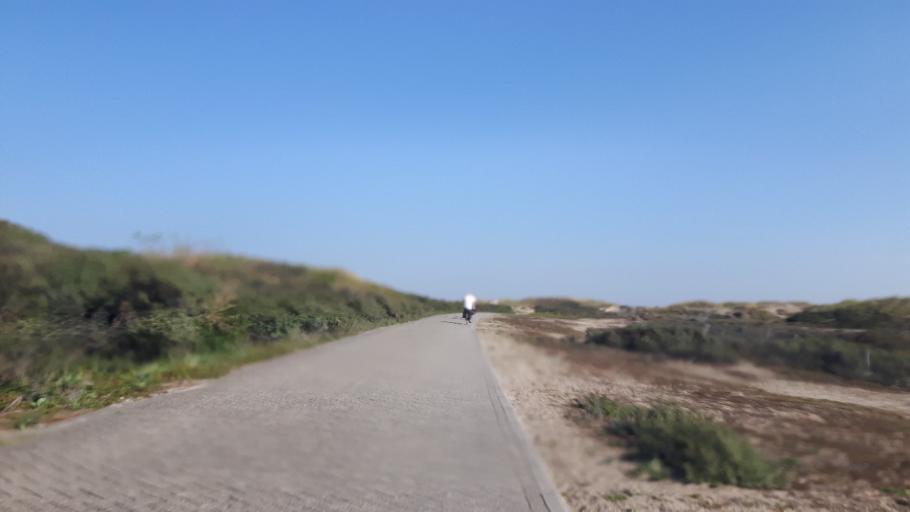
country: NL
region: South Holland
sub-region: Gemeente Noordwijkerhout
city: Noordwijkerhout
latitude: 52.2986
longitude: 4.4756
